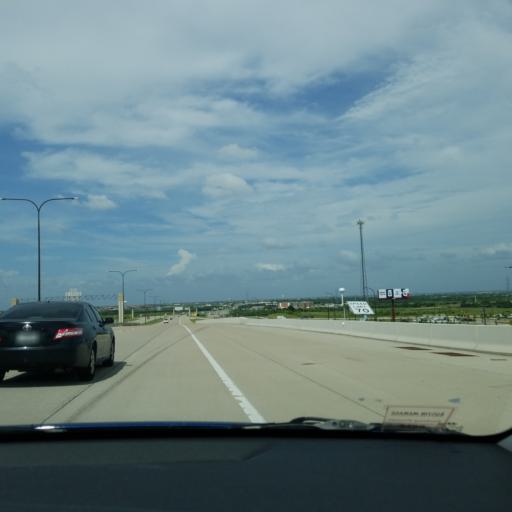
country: US
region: Texas
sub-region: Travis County
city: Manor
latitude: 30.3409
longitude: -97.5901
